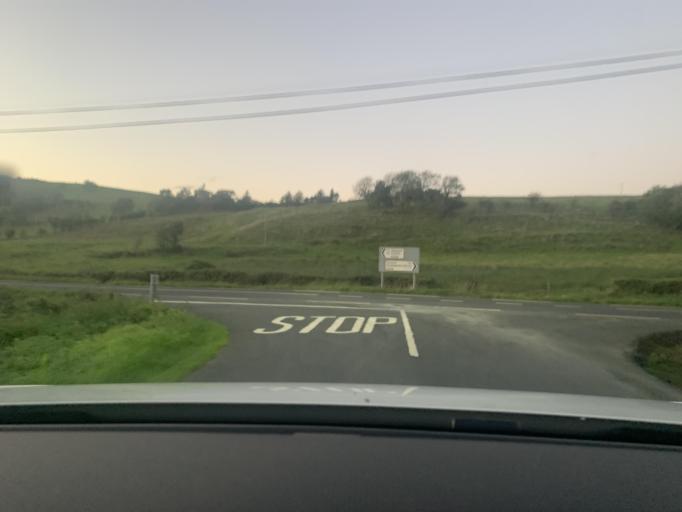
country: IE
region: Connaught
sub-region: County Leitrim
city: Manorhamilton
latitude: 54.2740
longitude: -8.2841
